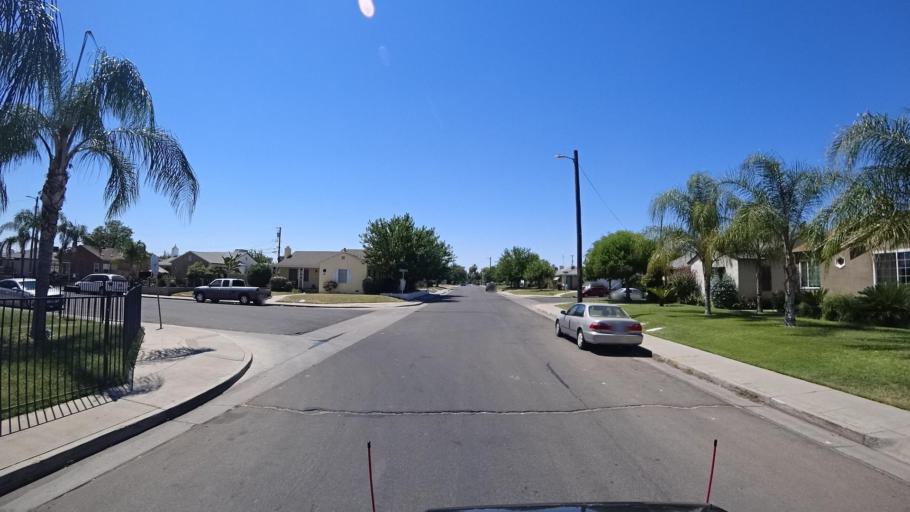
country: US
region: California
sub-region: Fresno County
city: Fresno
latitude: 36.7418
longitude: -119.7416
